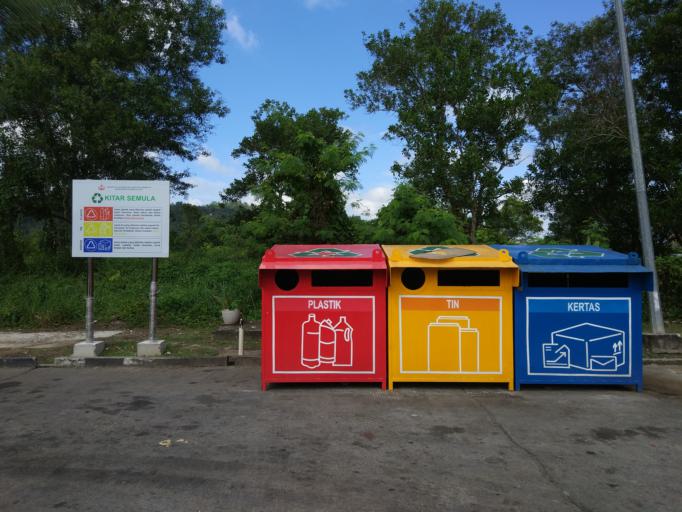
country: BN
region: Brunei and Muara
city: Bandar Seri Begawan
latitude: 4.8457
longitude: 114.8769
